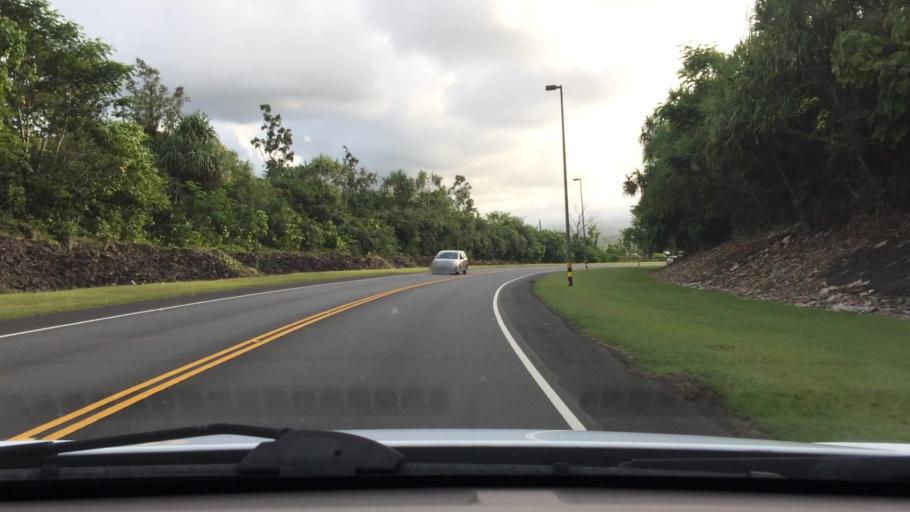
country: US
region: Hawaii
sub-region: Hawaii County
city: Hilo
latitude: 19.7116
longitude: -155.0583
